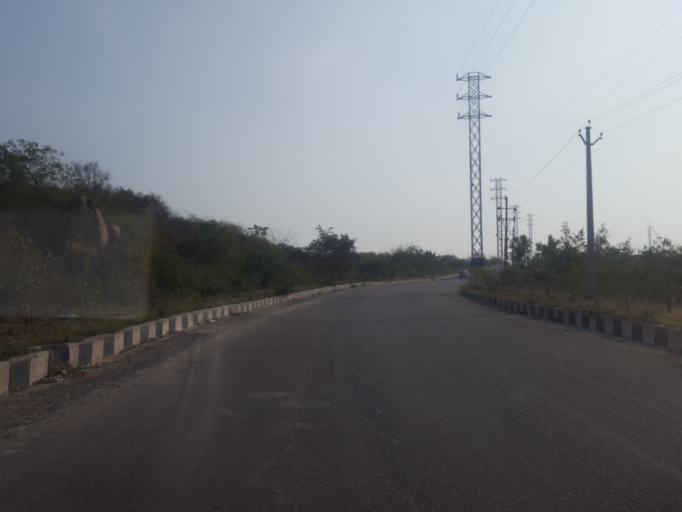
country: IN
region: Telangana
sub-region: Medak
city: Serilingampalle
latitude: 17.4067
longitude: 78.3157
